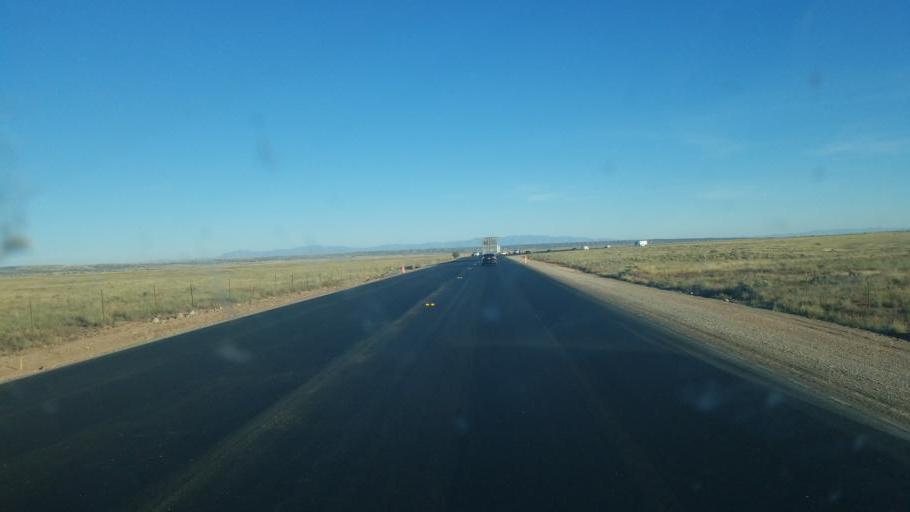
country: US
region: New Mexico
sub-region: Valencia County
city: Los Lunas
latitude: 34.8845
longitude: -107.0637
